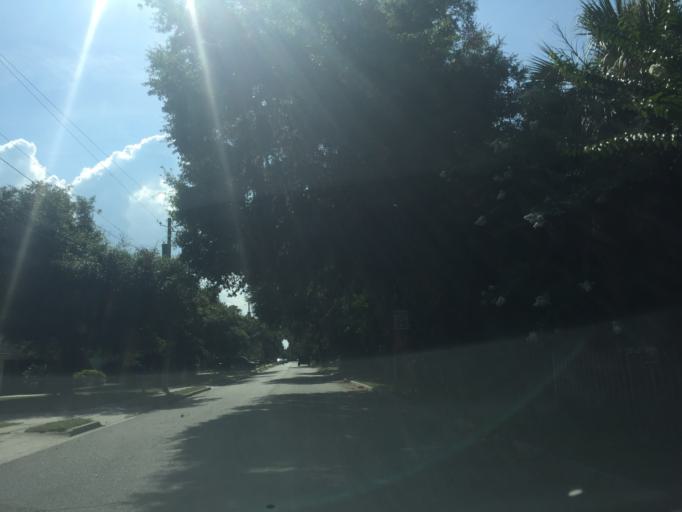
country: US
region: Georgia
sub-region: Chatham County
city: Isle of Hope
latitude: 31.9844
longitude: -81.0985
